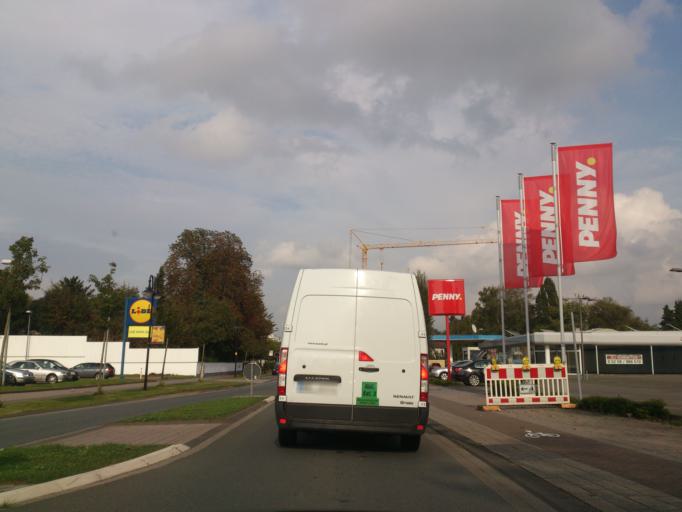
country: DE
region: North Rhine-Westphalia
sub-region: Regierungsbezirk Detmold
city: Salzkotten
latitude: 51.6695
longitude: 8.5968
